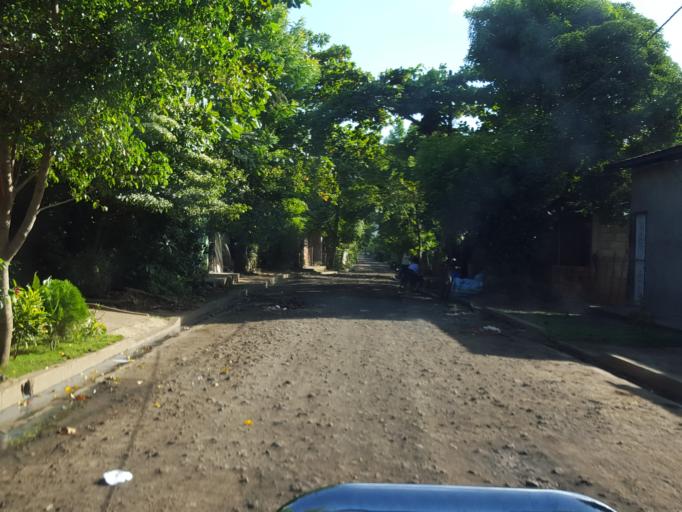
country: NI
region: Leon
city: Leon
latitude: 12.4252
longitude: -86.9079
